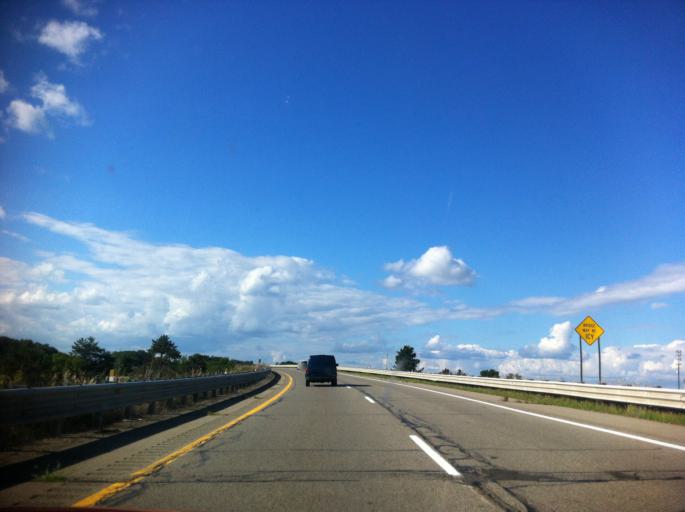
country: US
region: Michigan
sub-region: Washtenaw County
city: Ann Arbor
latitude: 42.3182
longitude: -83.7392
